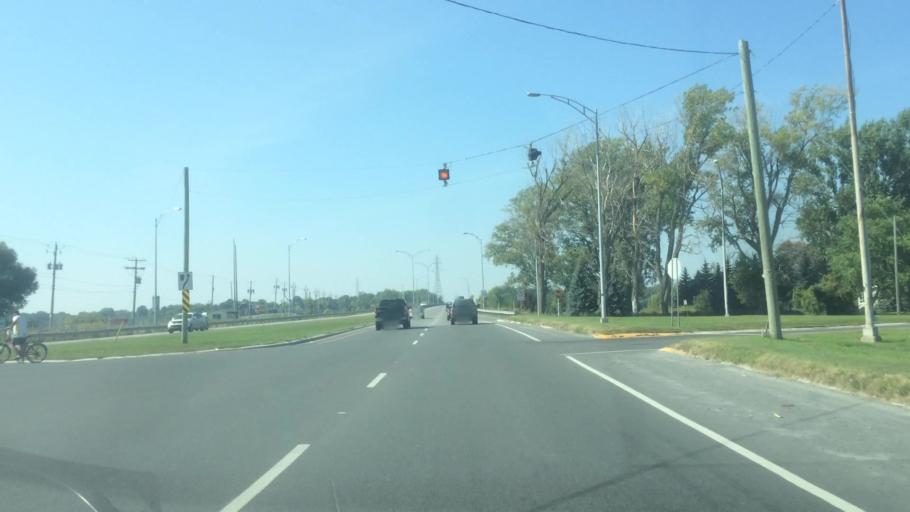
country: CA
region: Quebec
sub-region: Monteregie
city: Salaberry-de-Valleyfield
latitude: 45.2689
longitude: -74.1616
